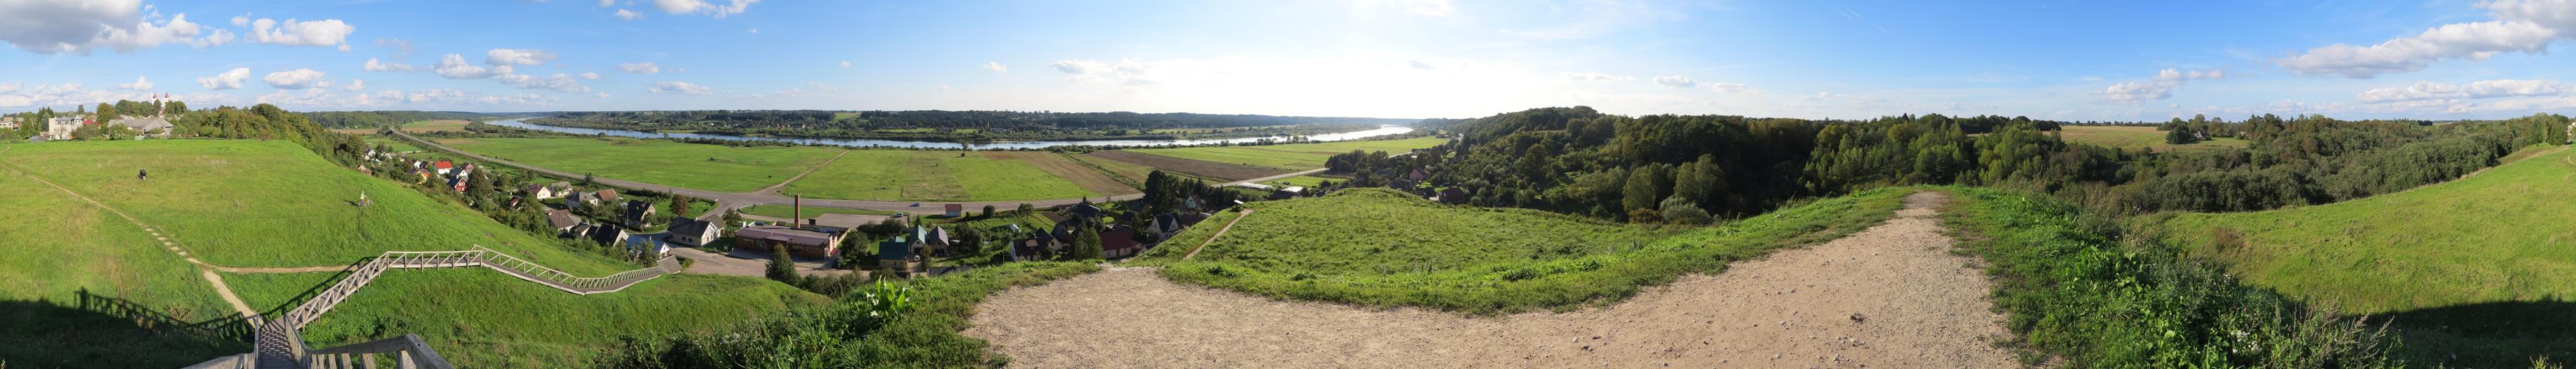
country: LT
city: Vilkija
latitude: 55.0803
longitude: 23.4068
